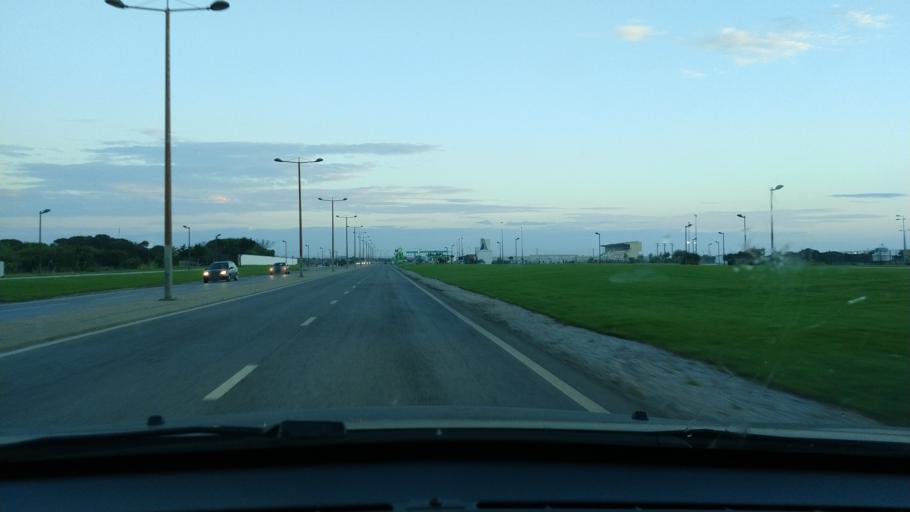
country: PT
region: Leiria
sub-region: Peniche
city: Peniche
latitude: 39.3563
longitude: -9.3641
